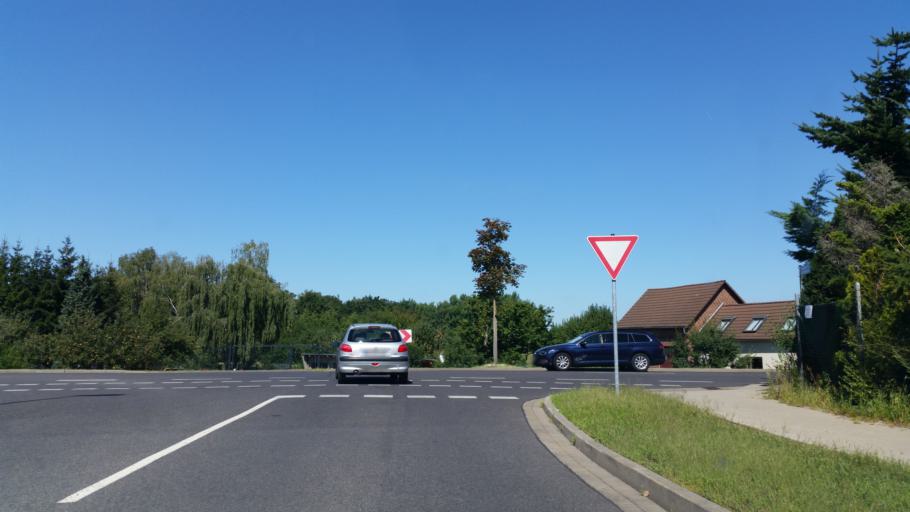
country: DE
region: Brandenburg
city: Cottbus
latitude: 51.7306
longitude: 14.3120
